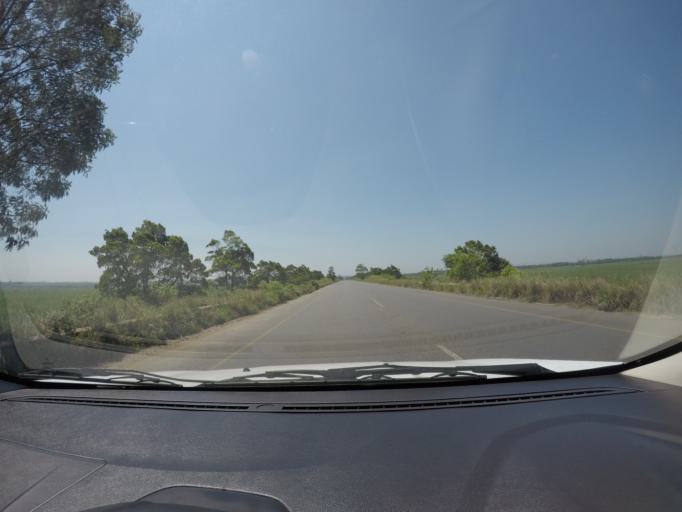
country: ZA
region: KwaZulu-Natal
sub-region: uThungulu District Municipality
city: Empangeni
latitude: -28.7947
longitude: 31.9583
